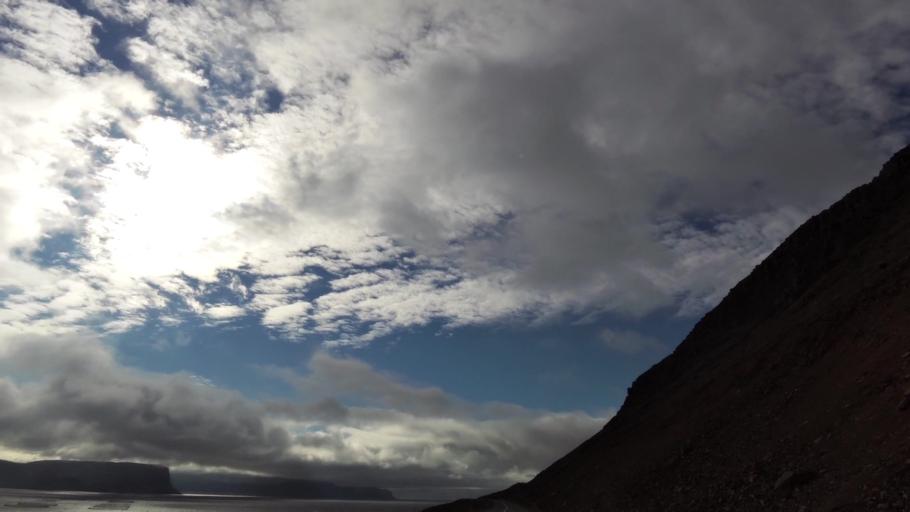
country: IS
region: West
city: Olafsvik
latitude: 65.5796
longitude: -23.9511
